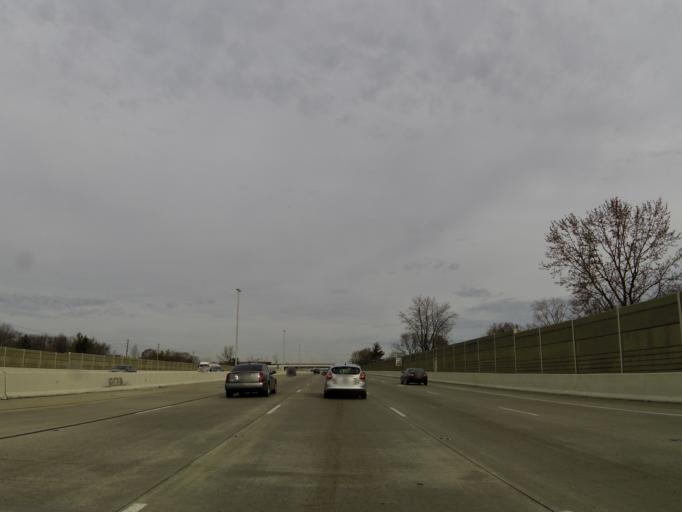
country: US
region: Indiana
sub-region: Marion County
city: Speedway
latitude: 39.8115
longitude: -86.2754
